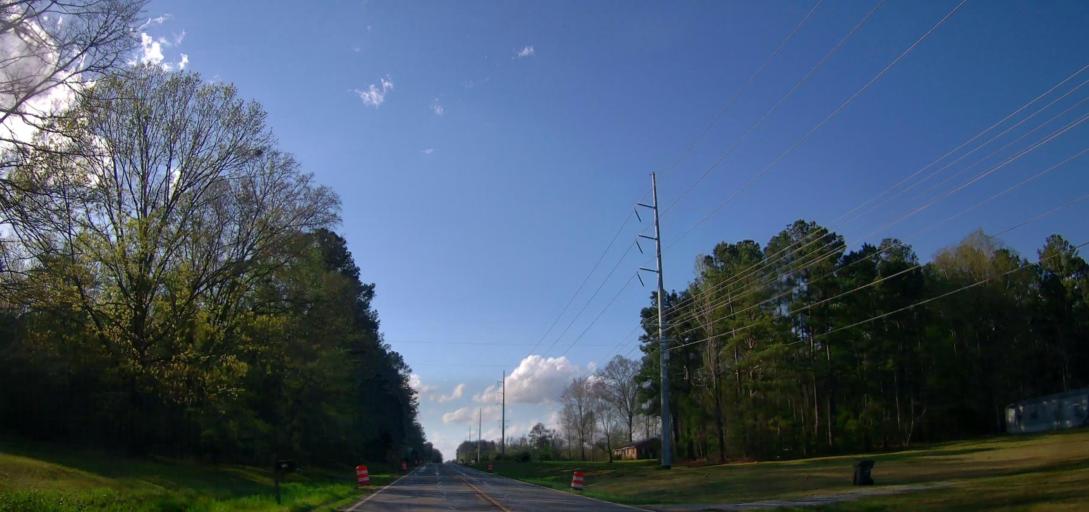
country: US
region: Georgia
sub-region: Baldwin County
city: Milledgeville
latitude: 33.1508
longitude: -83.3438
